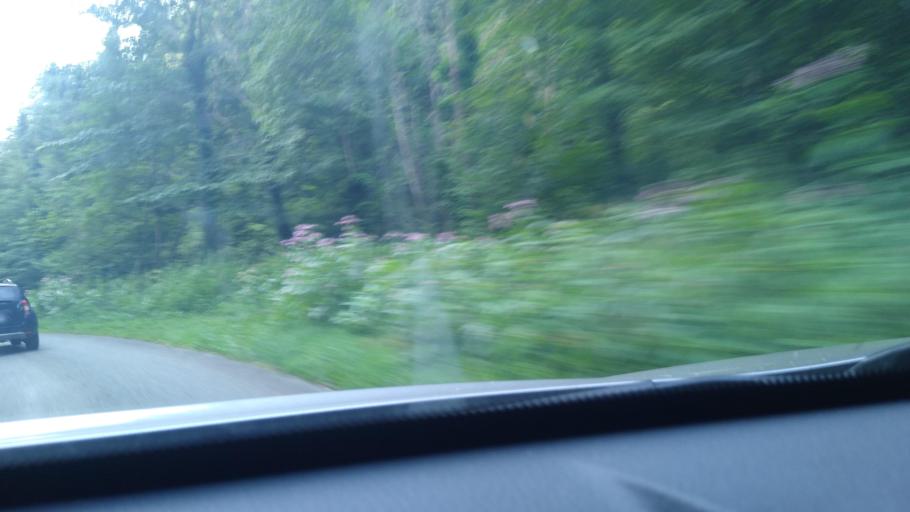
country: FR
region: Midi-Pyrenees
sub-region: Departement de l'Ariege
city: Saint-Girons
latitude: 42.8199
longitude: 1.1960
